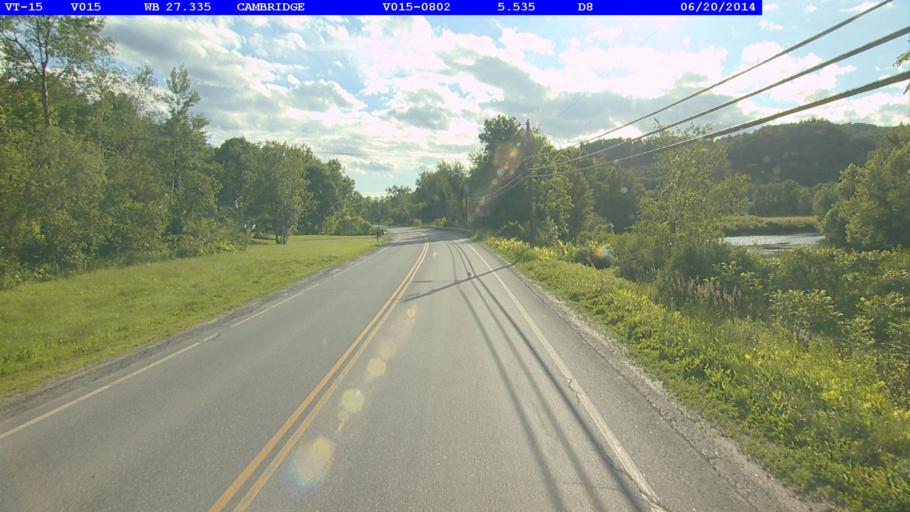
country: US
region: Vermont
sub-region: Lamoille County
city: Johnson
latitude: 44.6500
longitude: -72.8222
